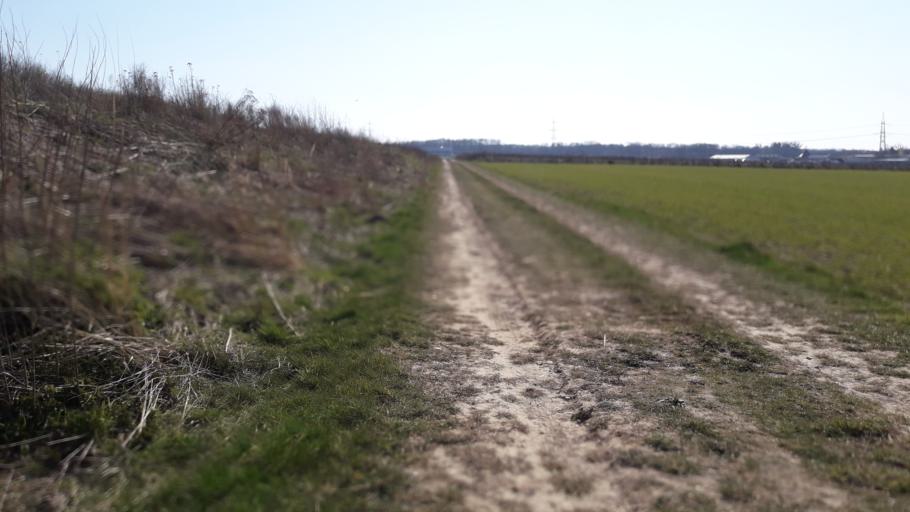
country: DE
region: North Rhine-Westphalia
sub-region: Regierungsbezirk Detmold
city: Paderborn
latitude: 51.6975
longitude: 8.7224
